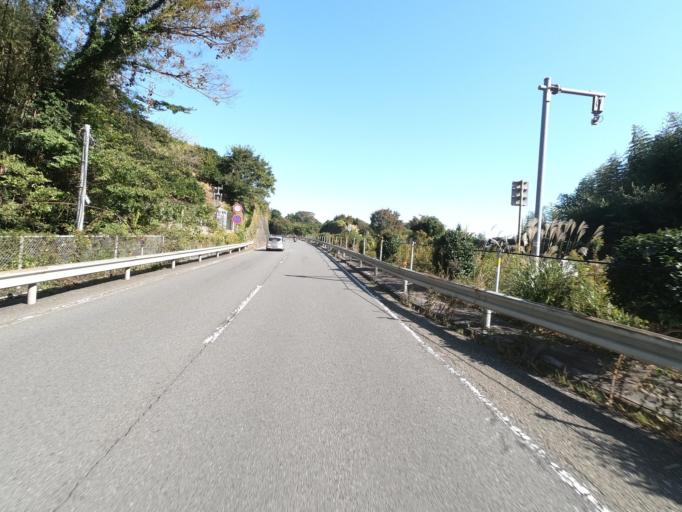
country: JP
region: Kanagawa
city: Ninomiya
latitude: 35.2972
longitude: 139.2147
